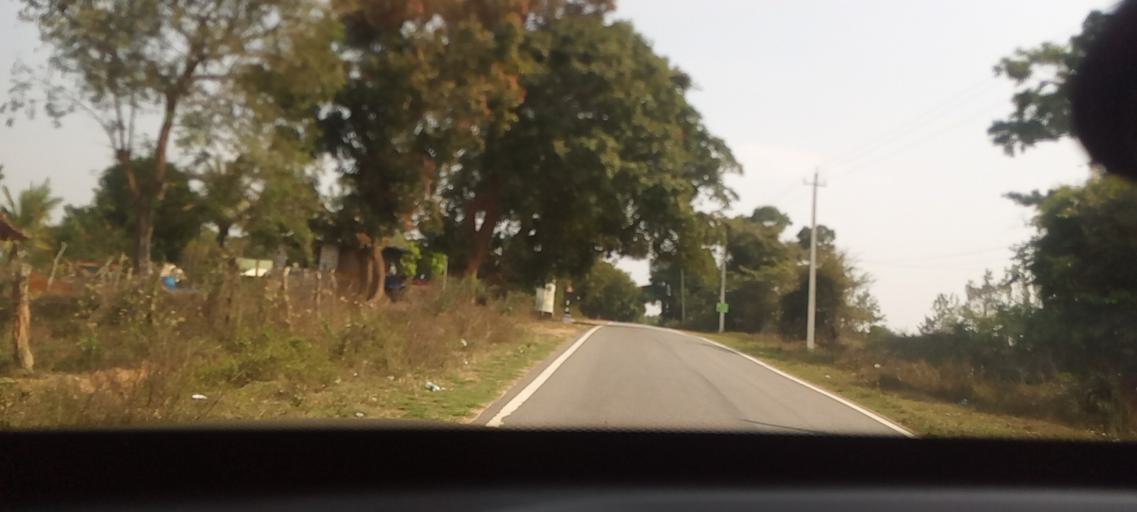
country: IN
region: Karnataka
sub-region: Hassan
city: Belur
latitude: 13.1843
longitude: 75.8013
